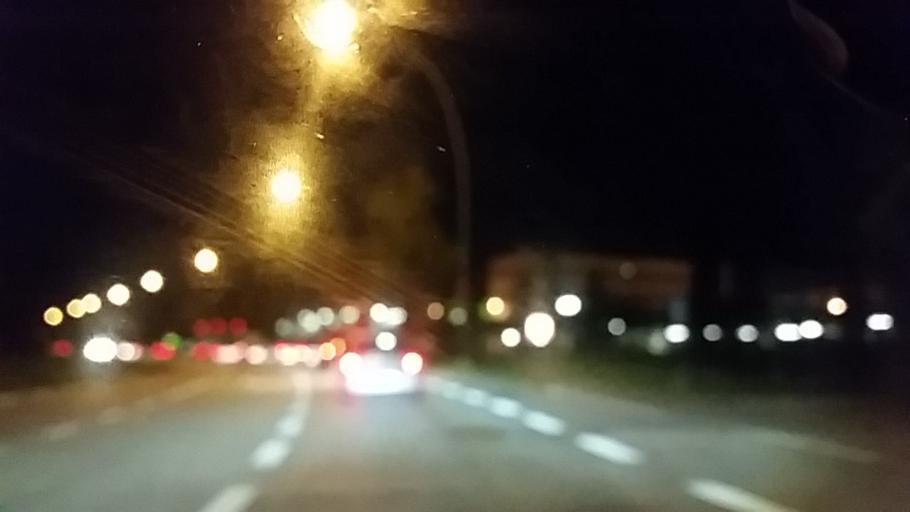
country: DE
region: Hamburg
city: Rothenburgsort
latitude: 53.5037
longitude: 10.0903
